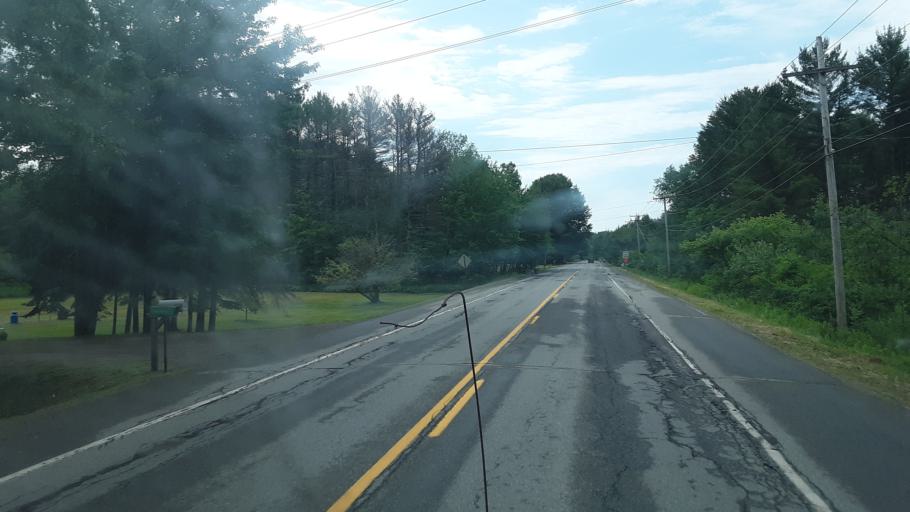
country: US
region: Maine
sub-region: Penobscot County
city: Eddington
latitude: 44.8317
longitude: -68.6952
